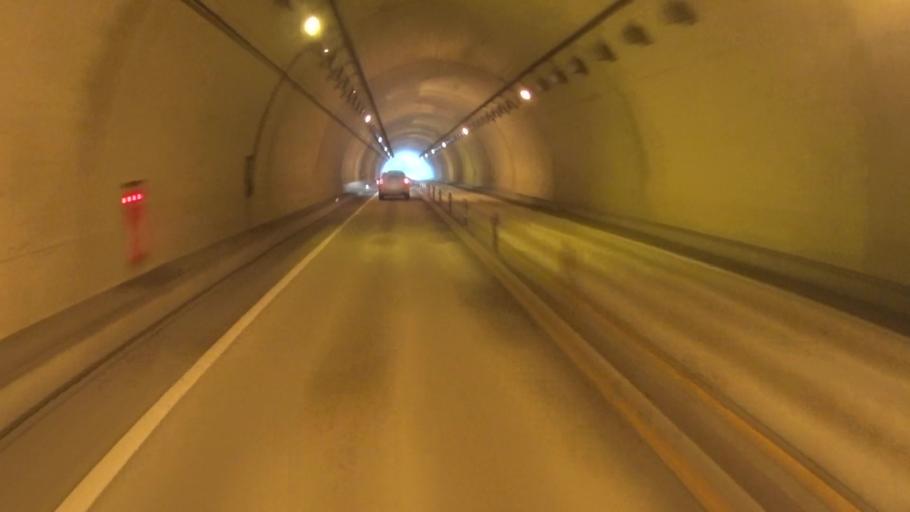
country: JP
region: Kyoto
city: Miyazu
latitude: 35.4578
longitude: 135.1767
